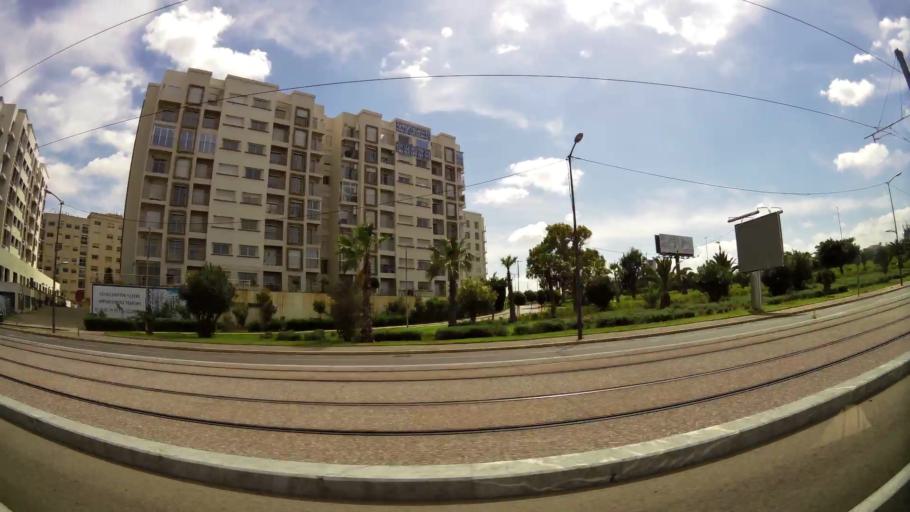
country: MA
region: Grand Casablanca
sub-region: Casablanca
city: Casablanca
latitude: 33.5530
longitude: -7.6319
